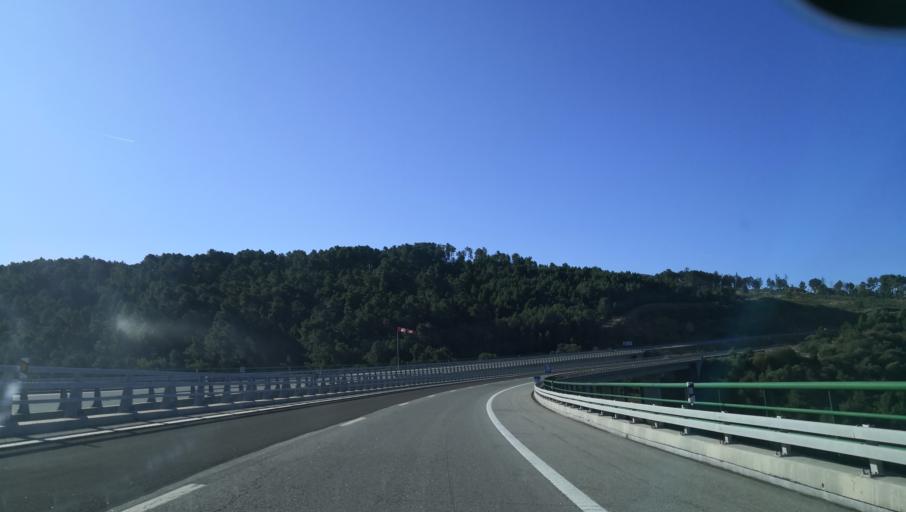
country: PT
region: Vila Real
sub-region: Vila Real
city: Vila Real
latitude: 41.3099
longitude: -7.6877
